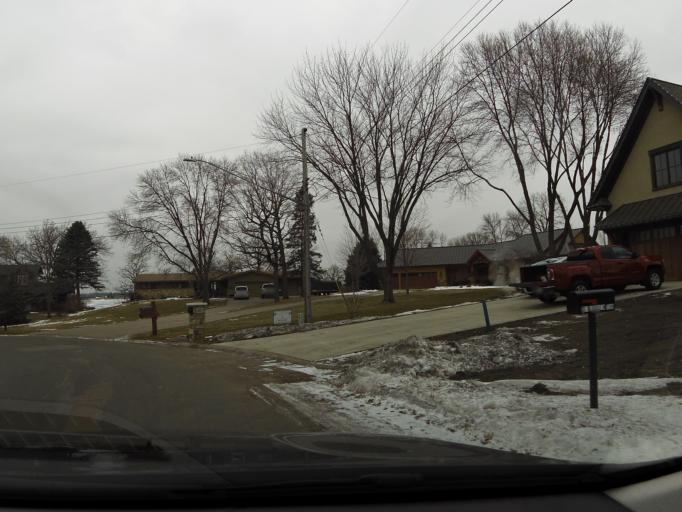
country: US
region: Minnesota
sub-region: Carver County
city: Waconia
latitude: 44.8615
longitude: -93.7980
